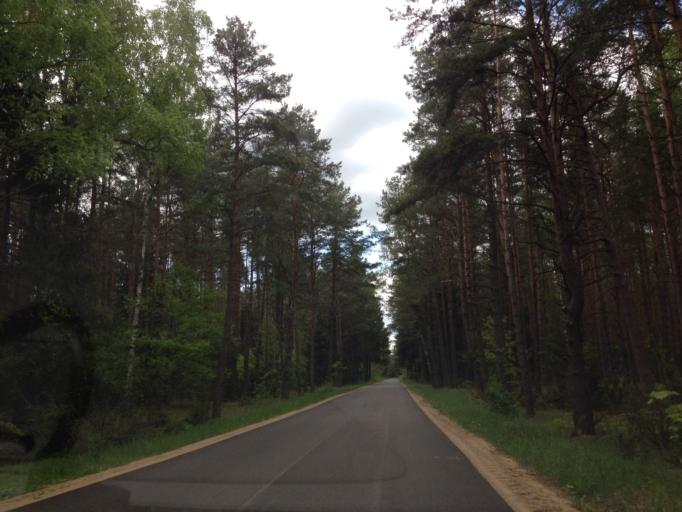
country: PL
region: Podlasie
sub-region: Powiat moniecki
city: Goniadz
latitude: 53.3537
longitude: 22.5985
